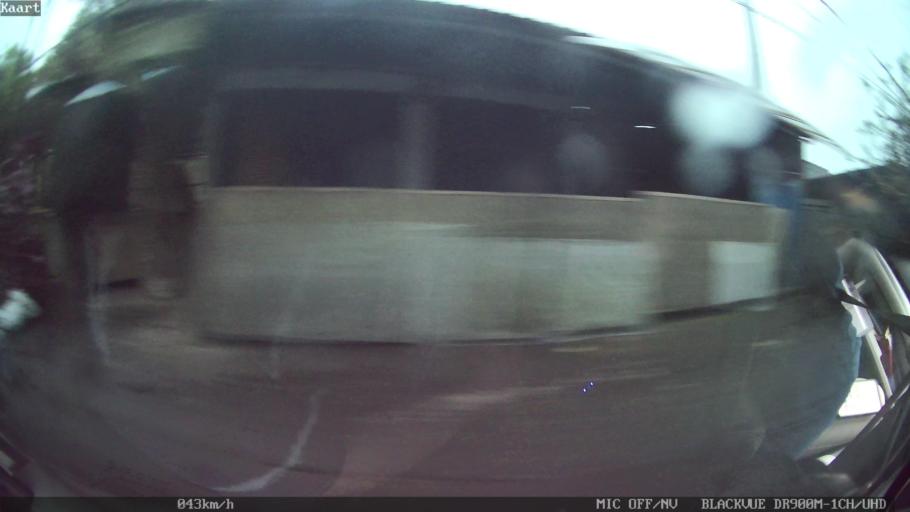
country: ID
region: Bali
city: Banjar Taro Kelod
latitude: -8.3358
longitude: 115.2852
